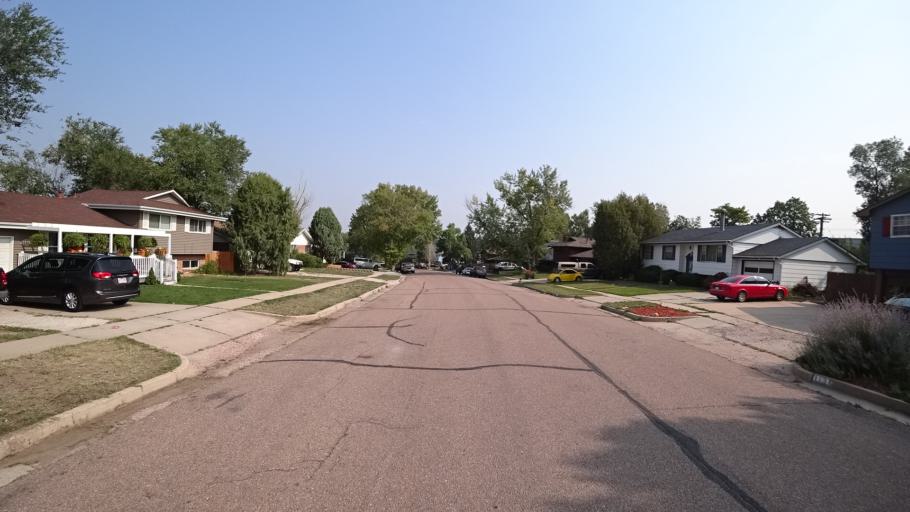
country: US
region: Colorado
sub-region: El Paso County
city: Stratmoor
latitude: 38.8160
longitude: -104.7744
